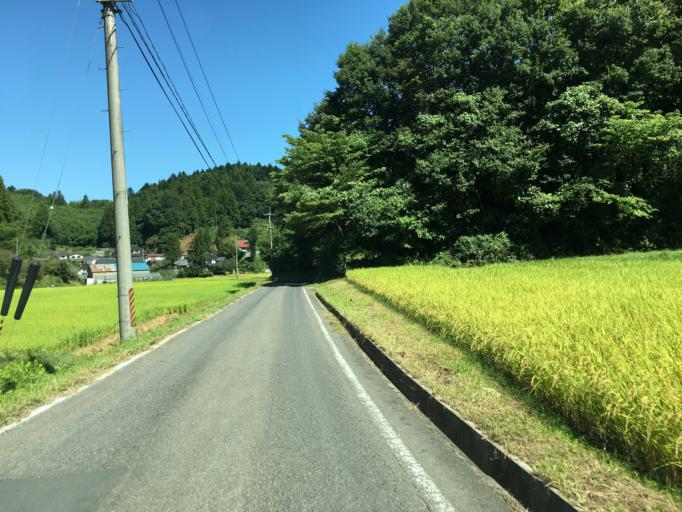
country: JP
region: Fukushima
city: Ishikawa
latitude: 37.2078
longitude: 140.5801
